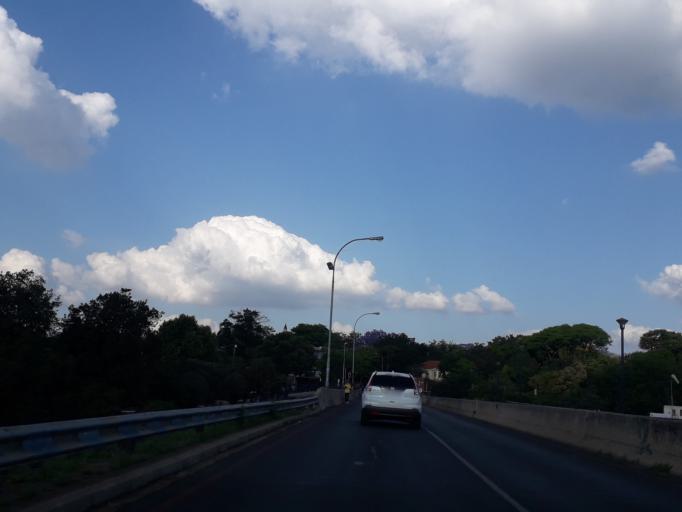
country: ZA
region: Gauteng
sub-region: City of Johannesburg Metropolitan Municipality
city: Johannesburg
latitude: -26.1504
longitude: 28.0050
